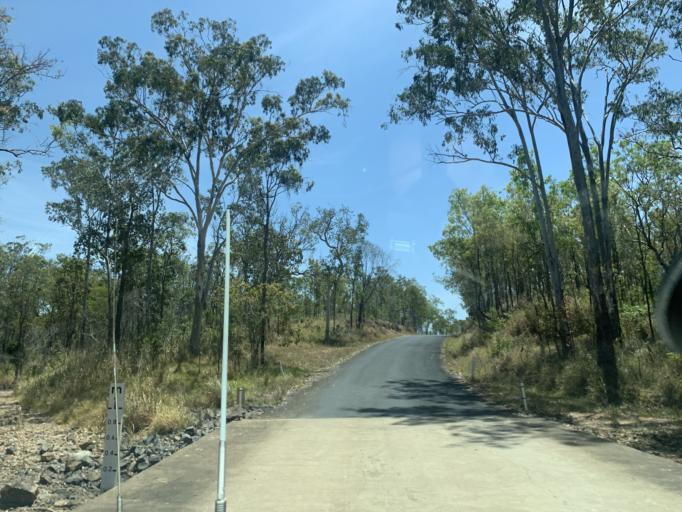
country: AU
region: Queensland
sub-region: Tablelands
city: Kuranda
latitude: -16.9114
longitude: 145.5745
